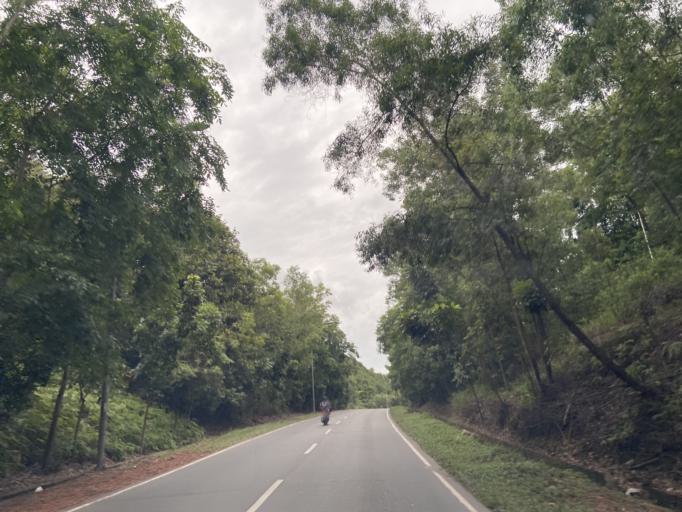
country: SG
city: Singapore
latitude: 1.1171
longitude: 104.0155
